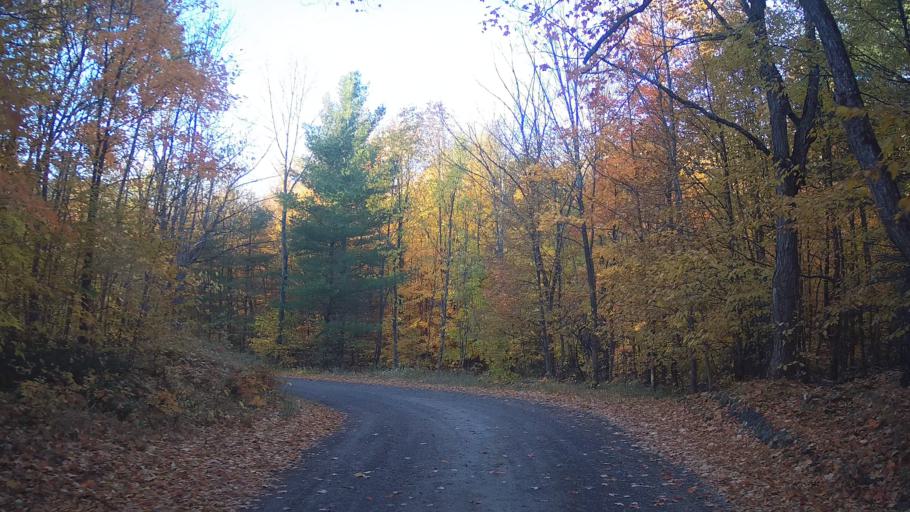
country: CA
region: Ontario
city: Arnprior
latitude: 45.3390
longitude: -76.3526
